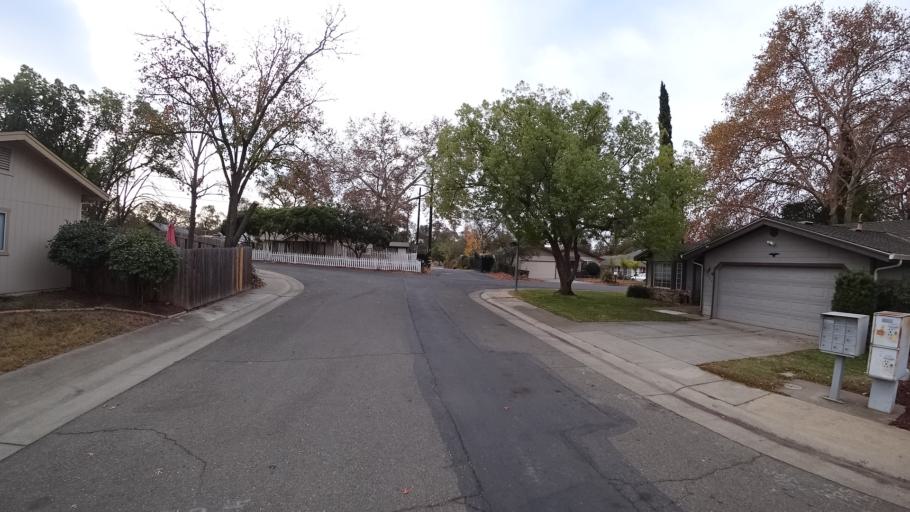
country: US
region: California
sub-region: Sacramento County
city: Citrus Heights
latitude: 38.7100
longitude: -121.2842
